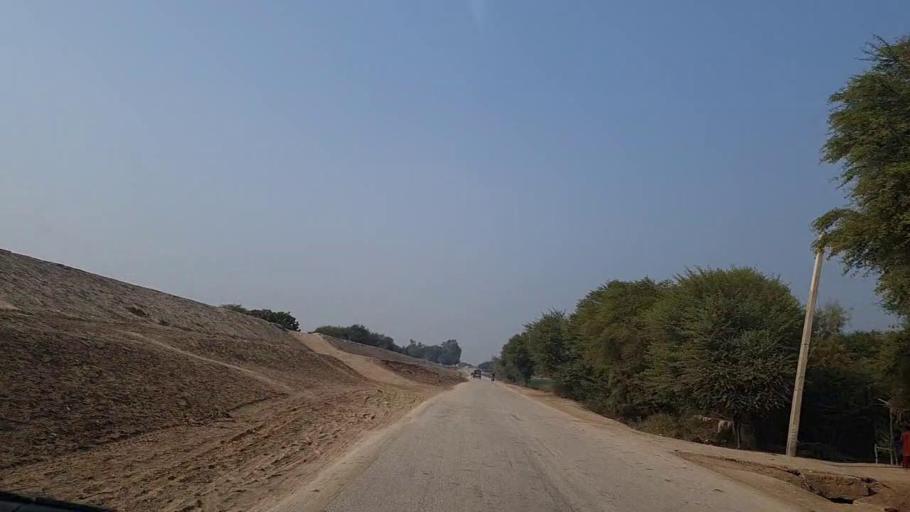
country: PK
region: Sindh
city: Sann
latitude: 26.1634
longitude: 68.1126
